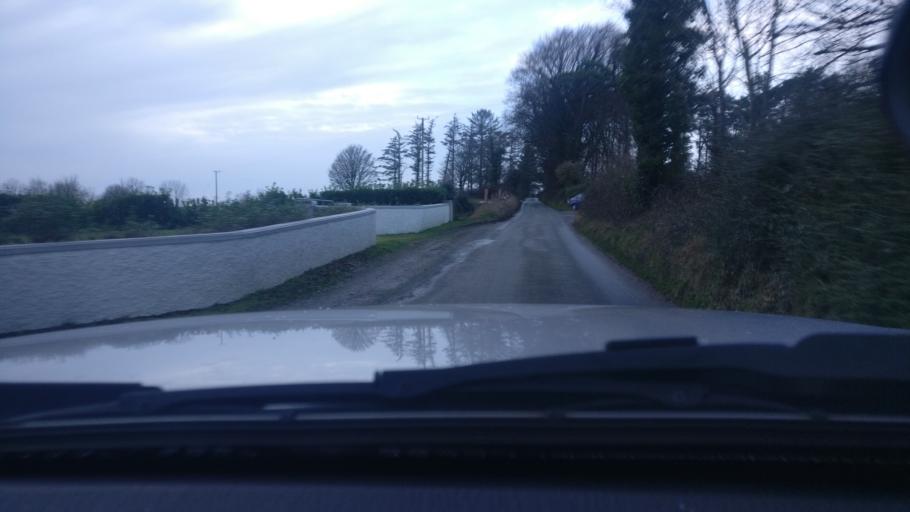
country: IE
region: Connaught
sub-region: County Galway
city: Loughrea
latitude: 53.1635
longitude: -8.5305
